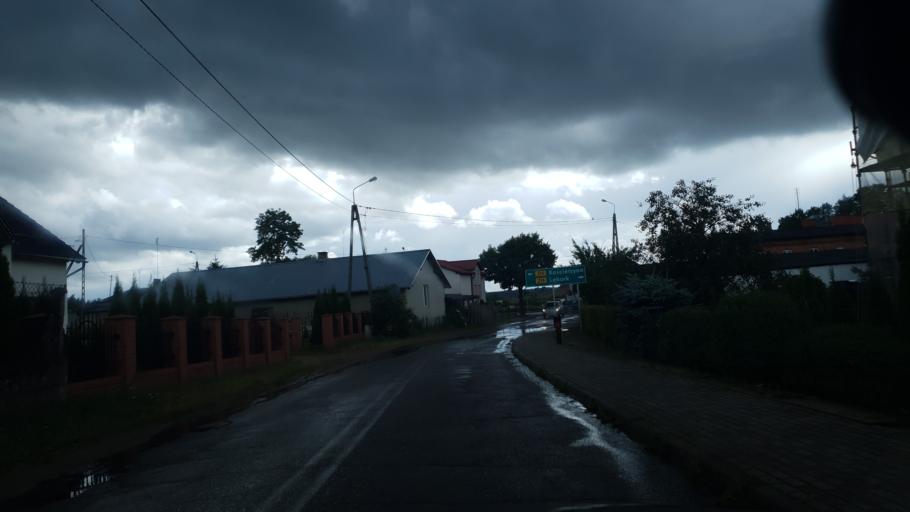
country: PL
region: Pomeranian Voivodeship
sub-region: Powiat kartuski
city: Stezyca
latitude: 54.2068
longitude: 17.9561
